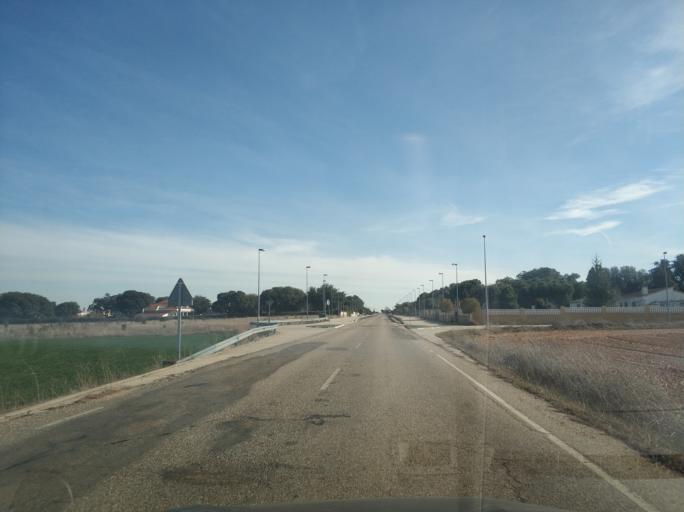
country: ES
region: Castille and Leon
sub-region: Provincia de Salamanca
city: Florida de Liebana
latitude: 41.0218
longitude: -5.7481
